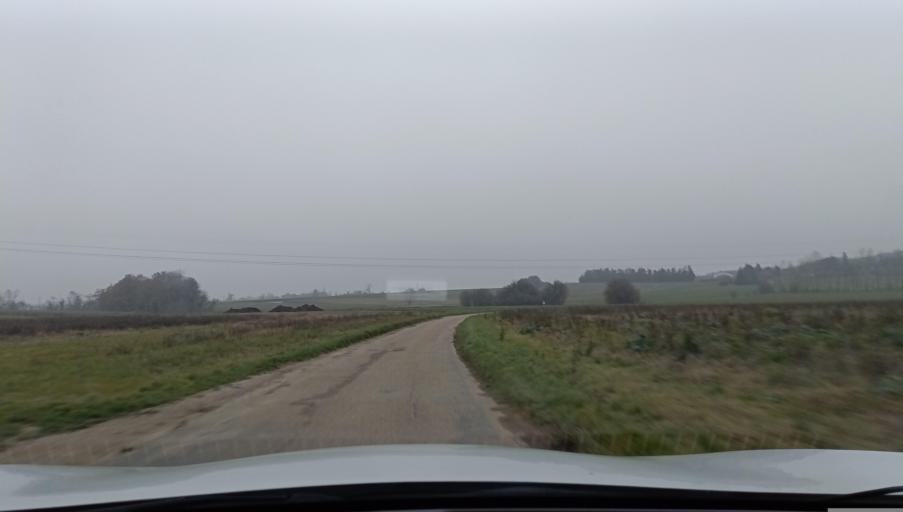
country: FR
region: Rhone-Alpes
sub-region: Departement de l'Isere
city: Seyssuel
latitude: 45.5780
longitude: 4.8496
